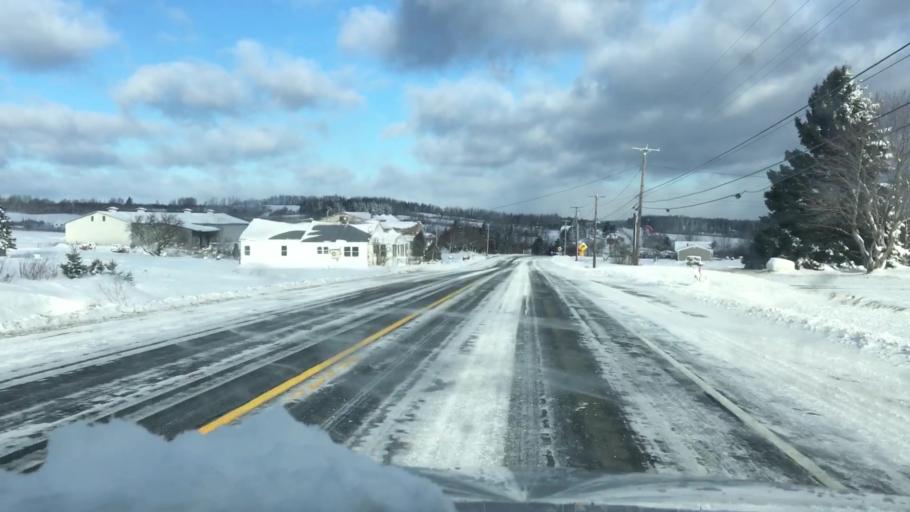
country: US
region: Maine
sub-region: Aroostook County
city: Caribou
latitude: 46.9527
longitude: -68.0257
